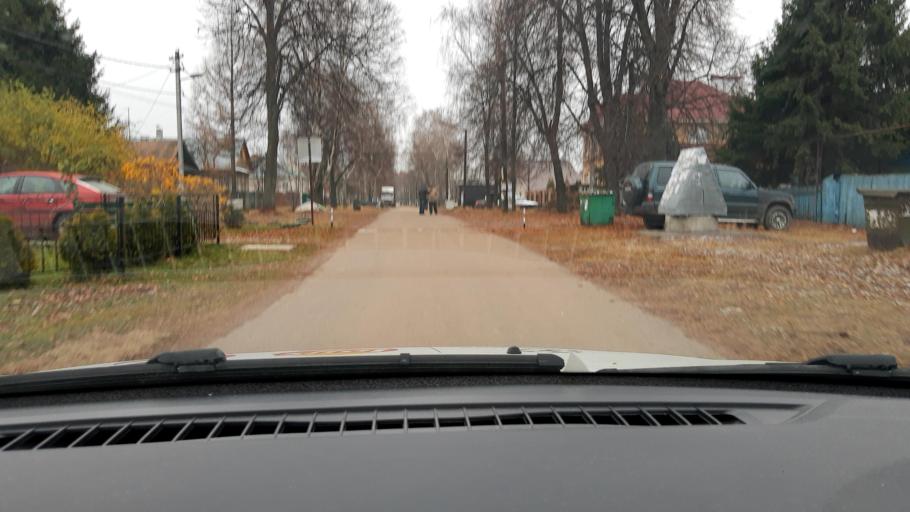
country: RU
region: Nizjnij Novgorod
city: Gorbatovka
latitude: 56.2046
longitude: 43.7666
